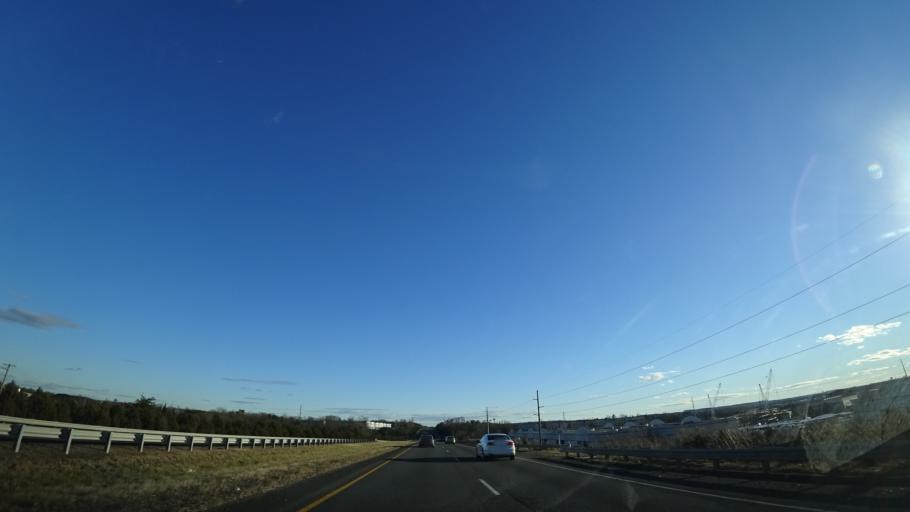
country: US
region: Virginia
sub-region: Prince William County
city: Bull Run
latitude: 38.7846
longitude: -77.5485
